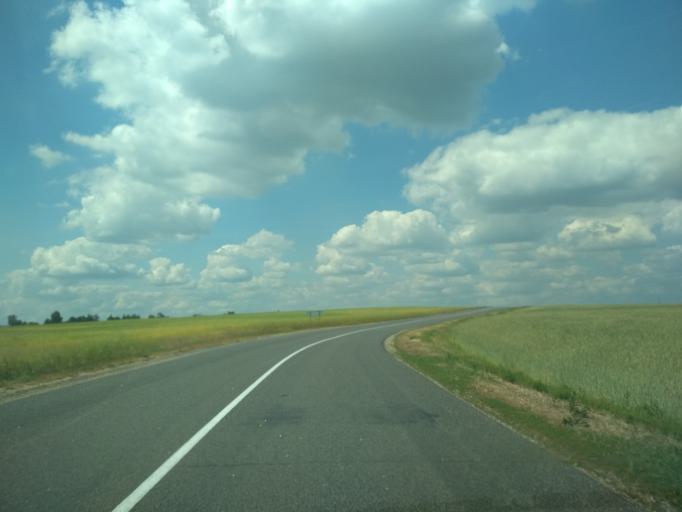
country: BY
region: Minsk
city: Mar''ina Horka
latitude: 53.5568
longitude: 28.0886
